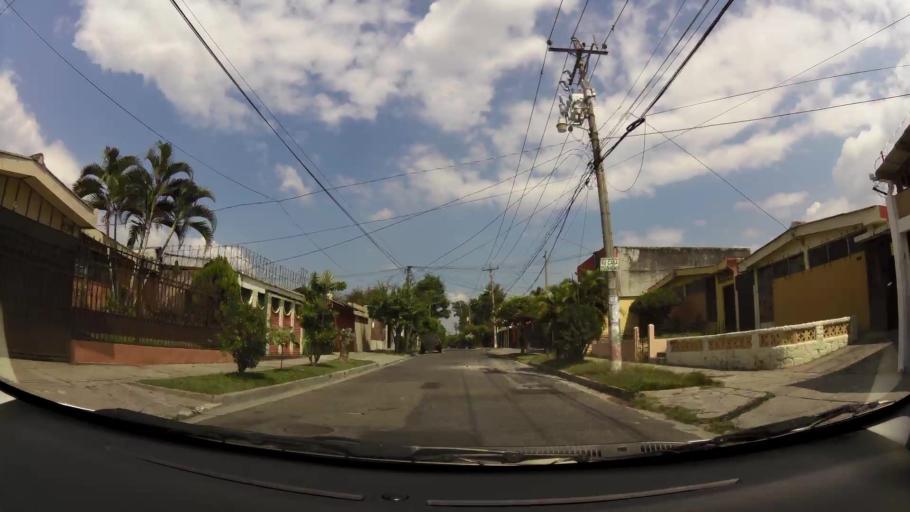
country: SV
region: San Salvador
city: Mejicanos
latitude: 13.7081
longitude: -89.2163
